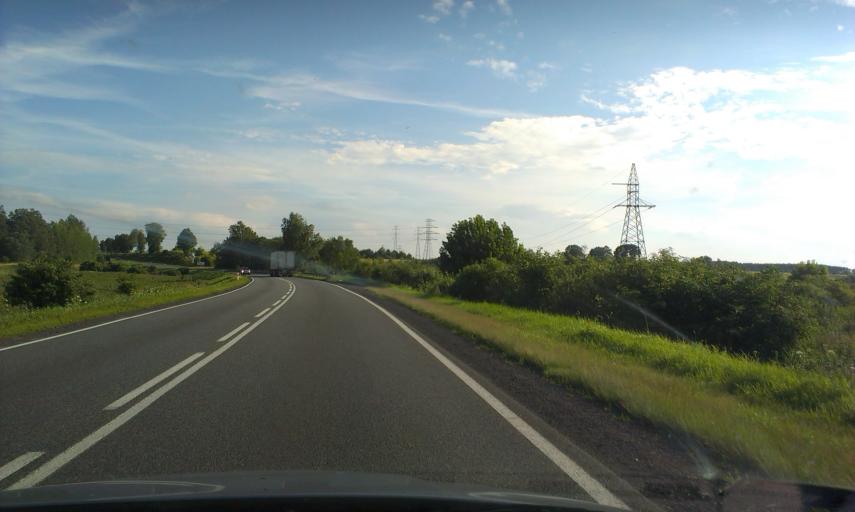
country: PL
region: Kujawsko-Pomorskie
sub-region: Powiat bydgoski
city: Biale Blota
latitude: 53.1407
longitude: 17.8793
